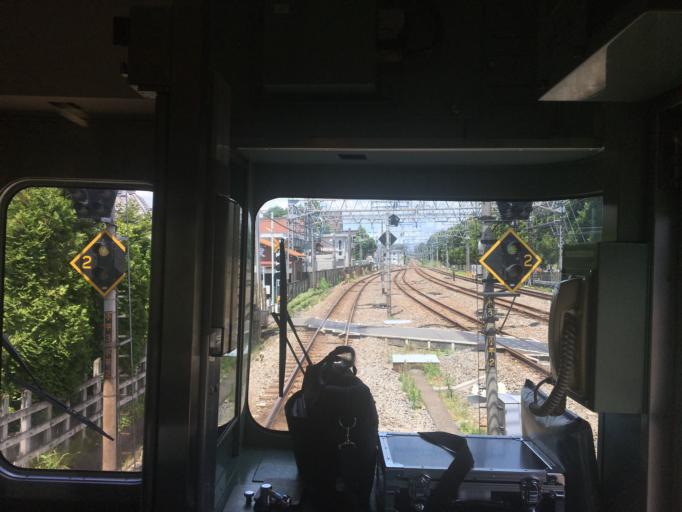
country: JP
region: Tokyo
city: Higashimurayama-shi
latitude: 35.7381
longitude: 139.4860
